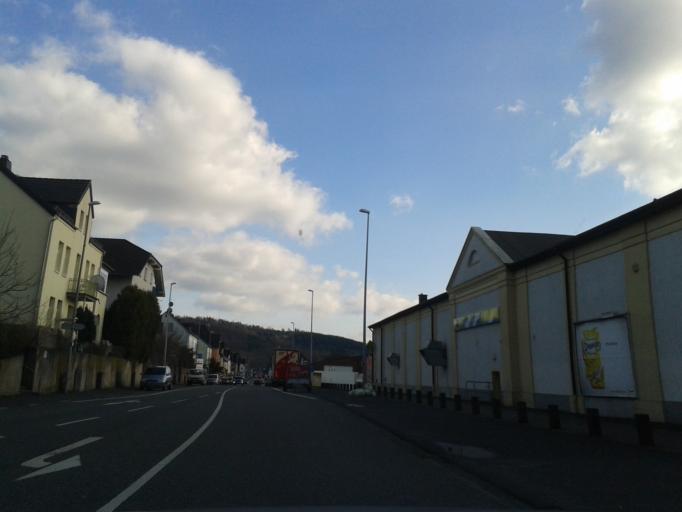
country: DE
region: Hesse
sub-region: Regierungsbezirk Giessen
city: Sinn
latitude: 50.6565
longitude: 8.3264
